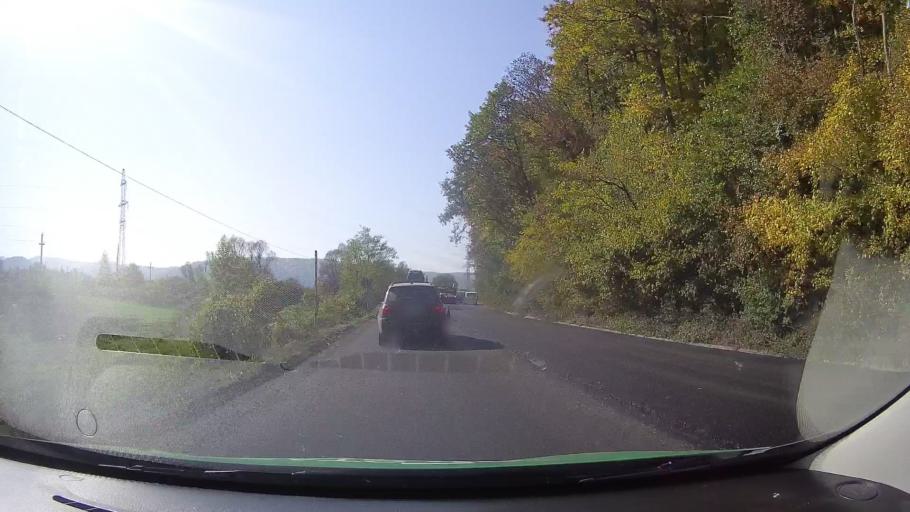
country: RO
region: Arad
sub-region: Comuna Petris
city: Petris
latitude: 46.0131
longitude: 22.3831
